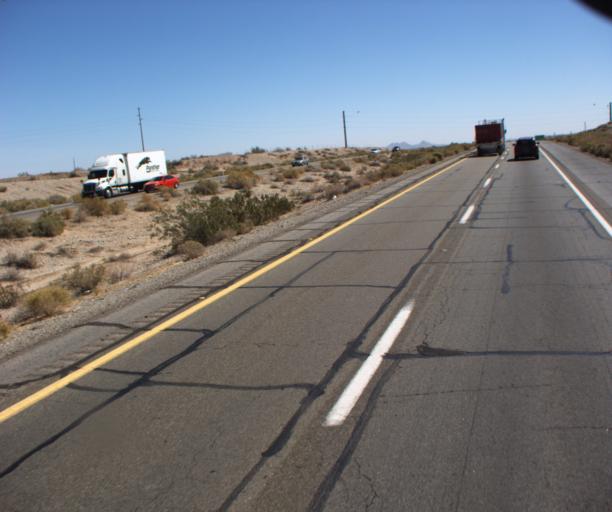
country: US
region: Arizona
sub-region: Yuma County
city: Wellton
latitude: 32.6619
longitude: -114.2634
